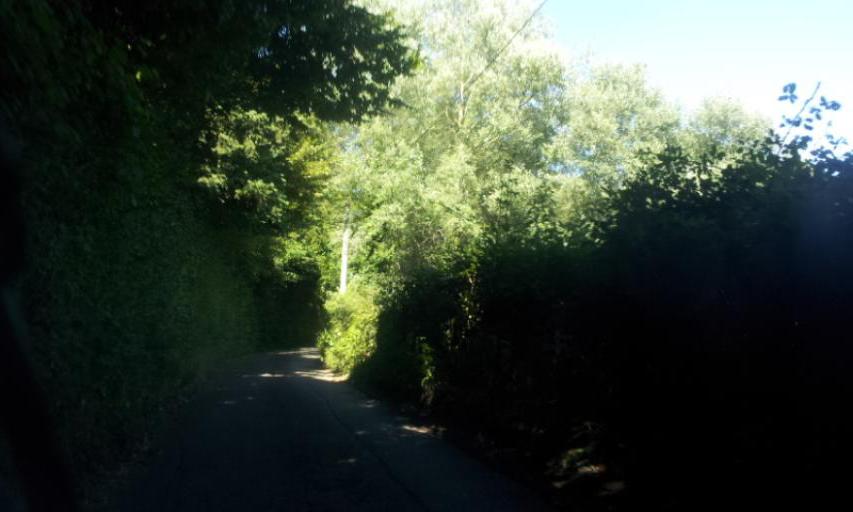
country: GB
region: England
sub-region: Kent
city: Sittingbourne
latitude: 51.3098
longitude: 0.7407
